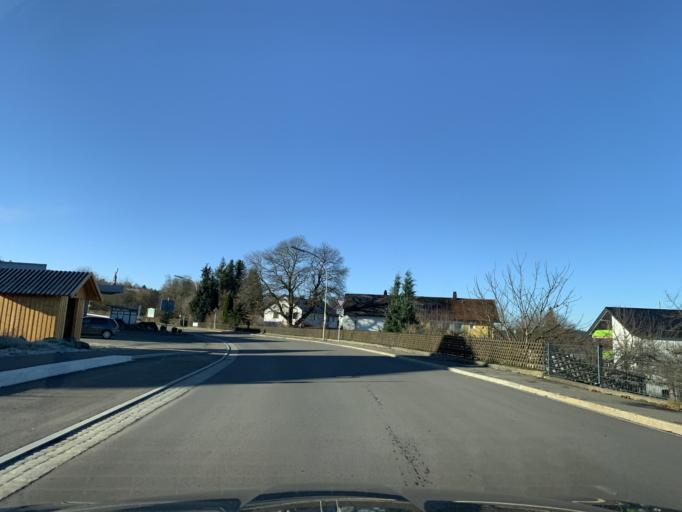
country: DE
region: Bavaria
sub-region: Upper Palatinate
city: Oberviechtach
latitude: 49.4525
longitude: 12.4184
